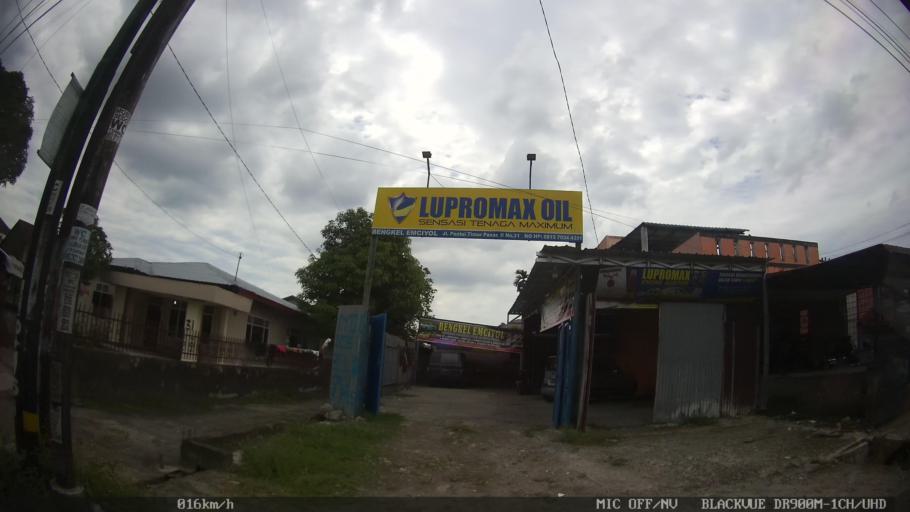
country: ID
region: North Sumatra
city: Sunggal
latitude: 3.5985
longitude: 98.6175
